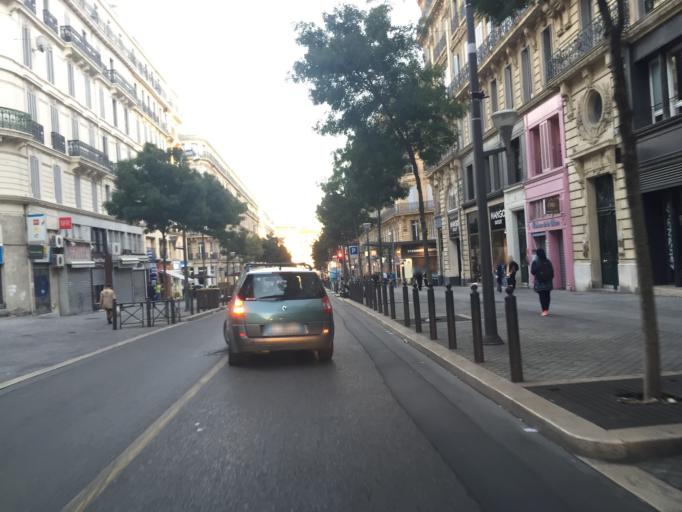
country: FR
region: Provence-Alpes-Cote d'Azur
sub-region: Departement des Bouches-du-Rhone
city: Marseille 02
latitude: 43.2983
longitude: 5.3725
